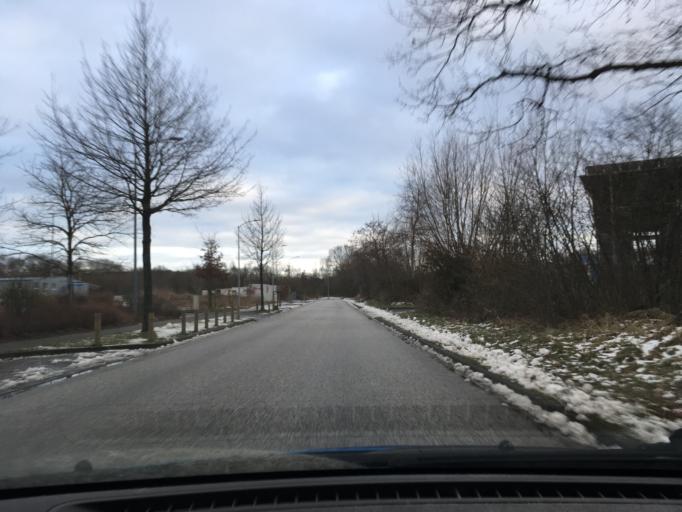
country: DE
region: Schleswig-Holstein
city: Ottenbuttel
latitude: 53.9591
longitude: 9.4982
